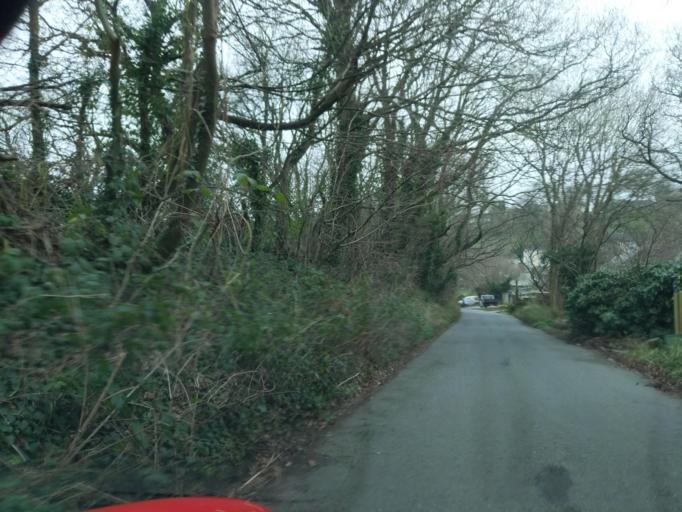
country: GB
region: England
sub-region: Plymouth
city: Plymstock
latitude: 50.3895
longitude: -4.0947
